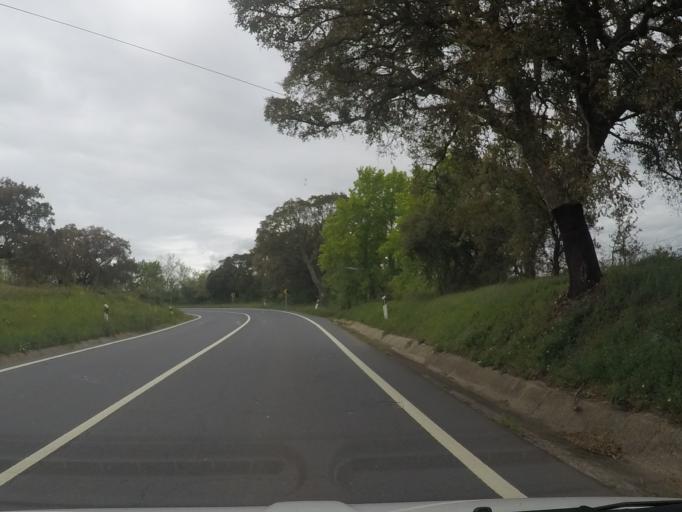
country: PT
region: Setubal
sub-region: Santiago do Cacem
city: Cercal
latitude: 37.8283
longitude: -8.6976
